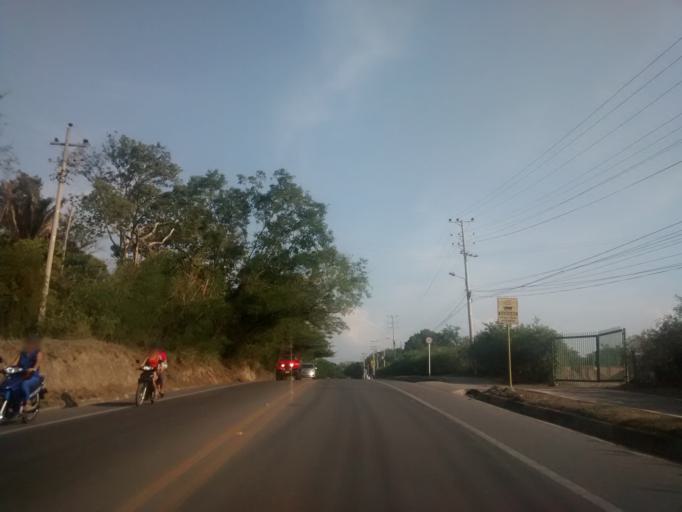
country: CO
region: Cundinamarca
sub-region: Girardot
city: Girardot City
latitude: 4.3008
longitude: -74.7931
